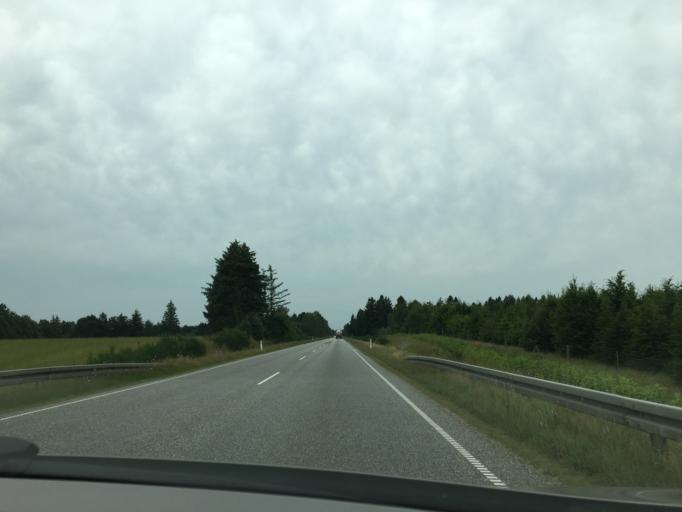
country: DK
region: Central Jutland
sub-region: Herning Kommune
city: Sunds
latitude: 56.3681
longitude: 8.9803
